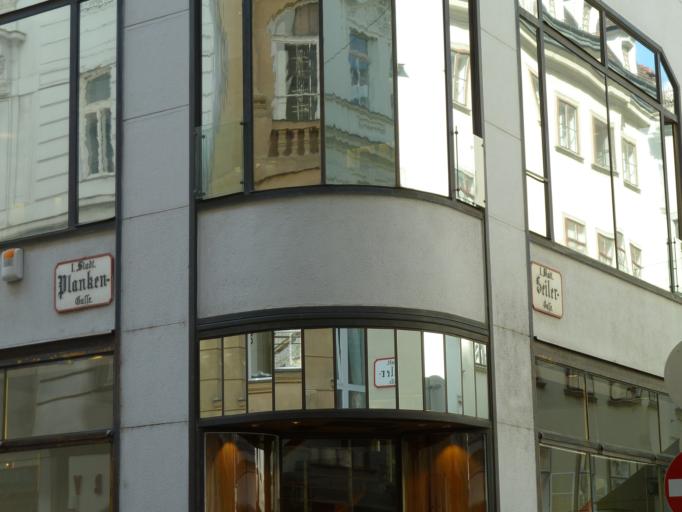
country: AT
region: Vienna
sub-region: Wien Stadt
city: Vienna
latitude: 48.2063
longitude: 16.3702
